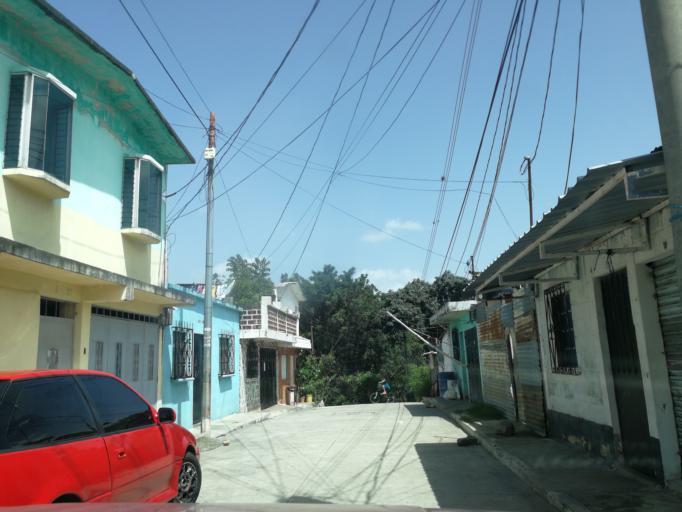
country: GT
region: Guatemala
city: Santa Catarina Pinula
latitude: 14.5475
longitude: -90.5190
